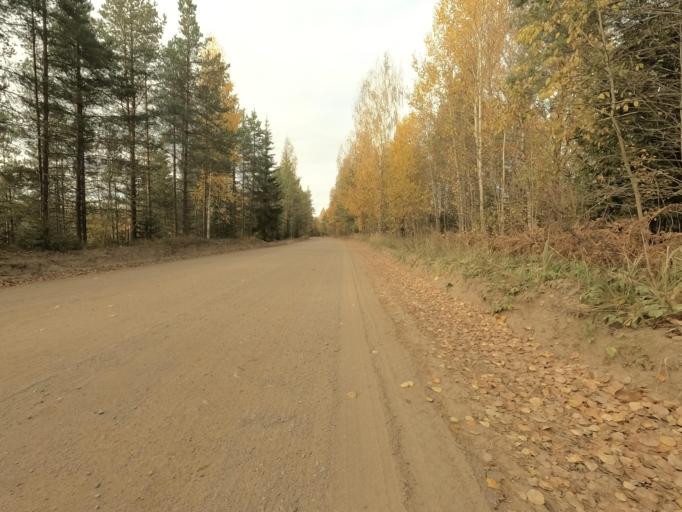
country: RU
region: Leningrad
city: Priladozhskiy
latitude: 59.6792
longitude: 31.3645
